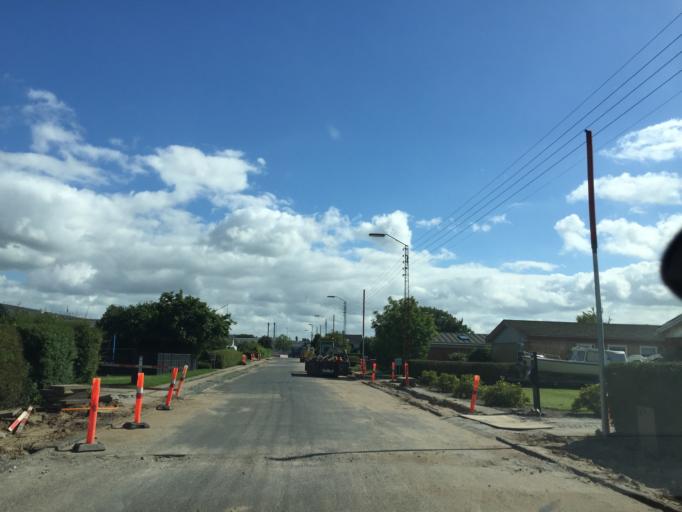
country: DK
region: South Denmark
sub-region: Odense Kommune
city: Hojby
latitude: 55.3586
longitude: 10.4026
